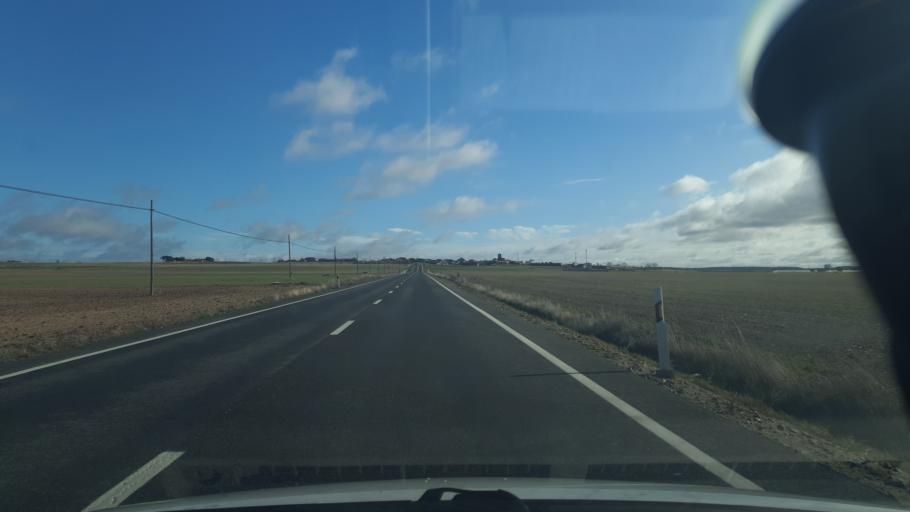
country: ES
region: Castille and Leon
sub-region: Provincia de Segovia
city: Martin Munoz de la Dehesa
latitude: 41.0469
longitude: -4.6456
